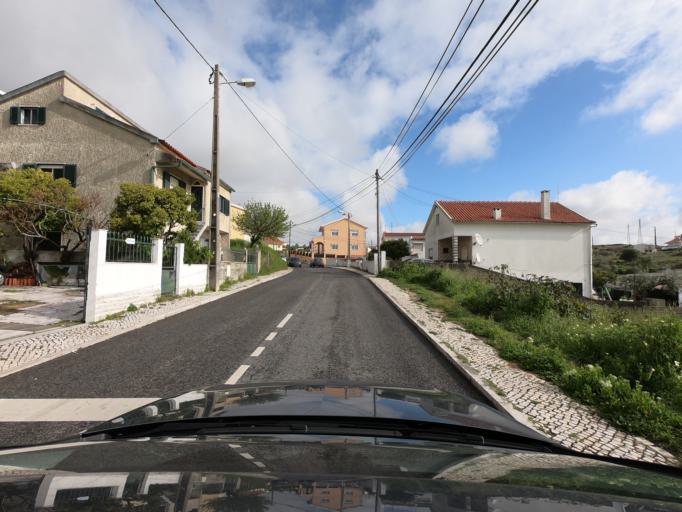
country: PT
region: Lisbon
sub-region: Oeiras
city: Porto Salvo
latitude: 38.7265
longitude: -9.3099
